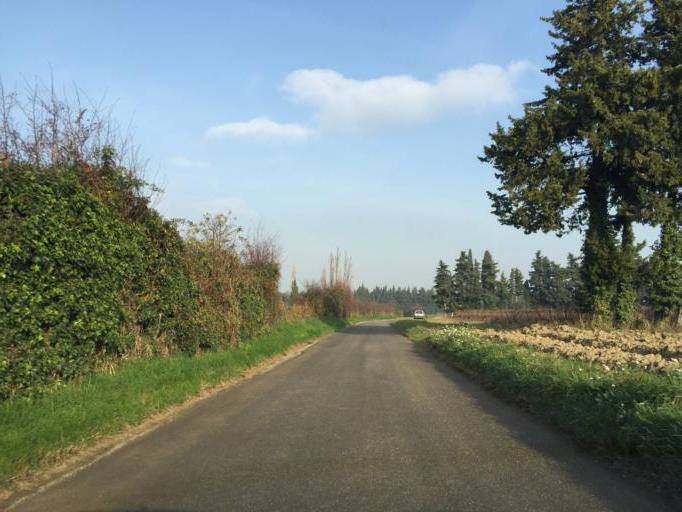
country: FR
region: Provence-Alpes-Cote d'Azur
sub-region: Departement du Vaucluse
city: Courthezon
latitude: 44.0748
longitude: 4.9059
